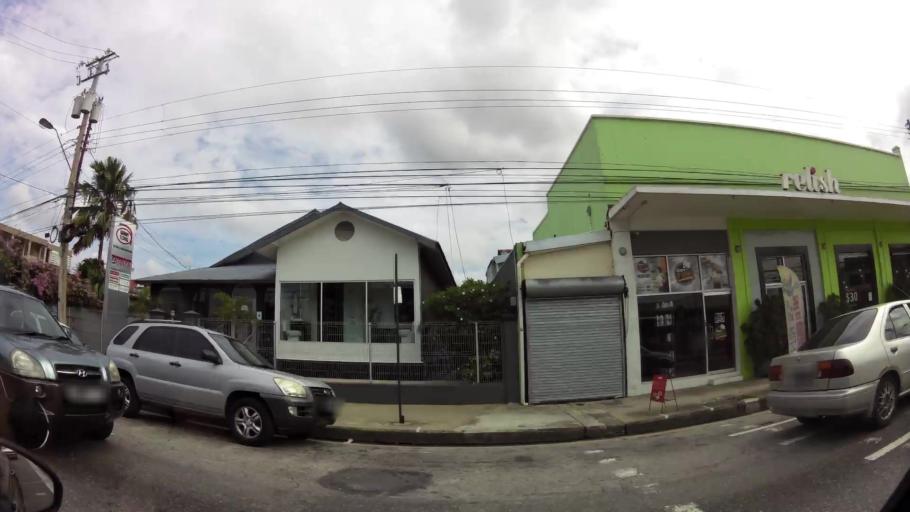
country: TT
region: City of Port of Spain
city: Port-of-Spain
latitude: 10.6591
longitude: -61.5198
